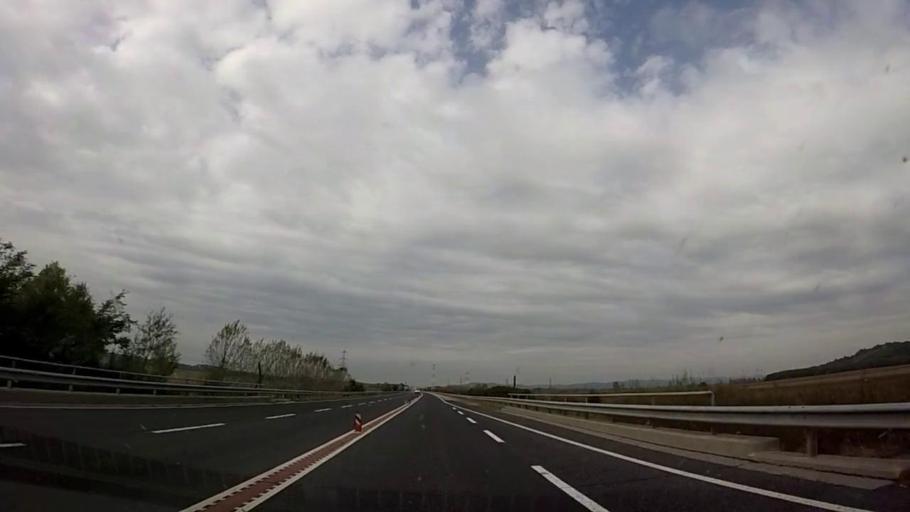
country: HR
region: Medimurska
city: Domasinec
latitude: 46.5036
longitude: 16.6051
